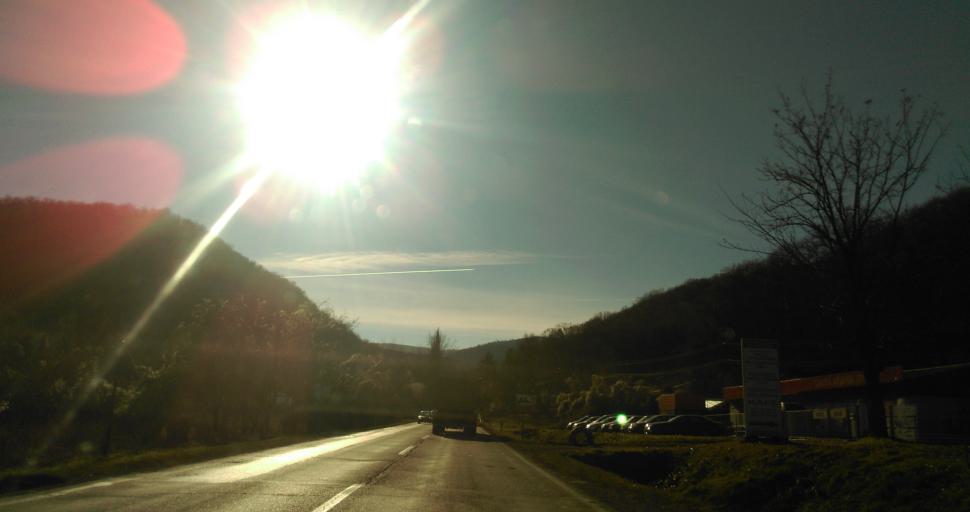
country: RS
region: Autonomna Pokrajina Vojvodina
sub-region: Juznobacki Okrug
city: Novi Sad
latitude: 45.1877
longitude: 19.8402
